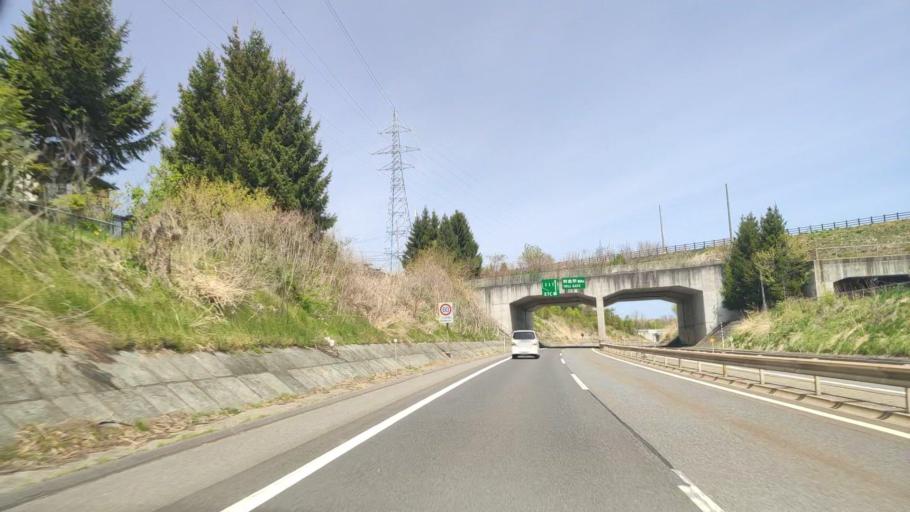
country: JP
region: Aomori
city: Hachinohe
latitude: 40.4780
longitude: 141.4594
